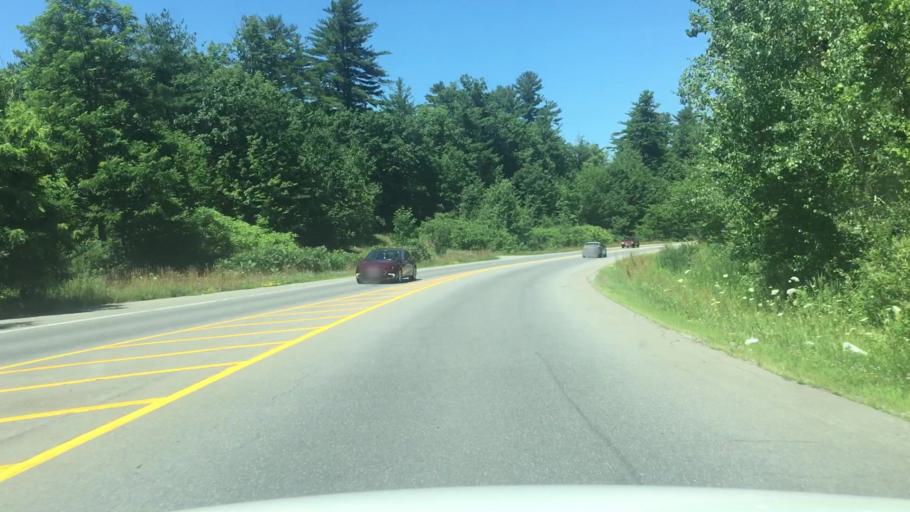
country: US
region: Maine
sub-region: Kennebec County
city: Waterville
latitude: 44.5344
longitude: -69.6505
